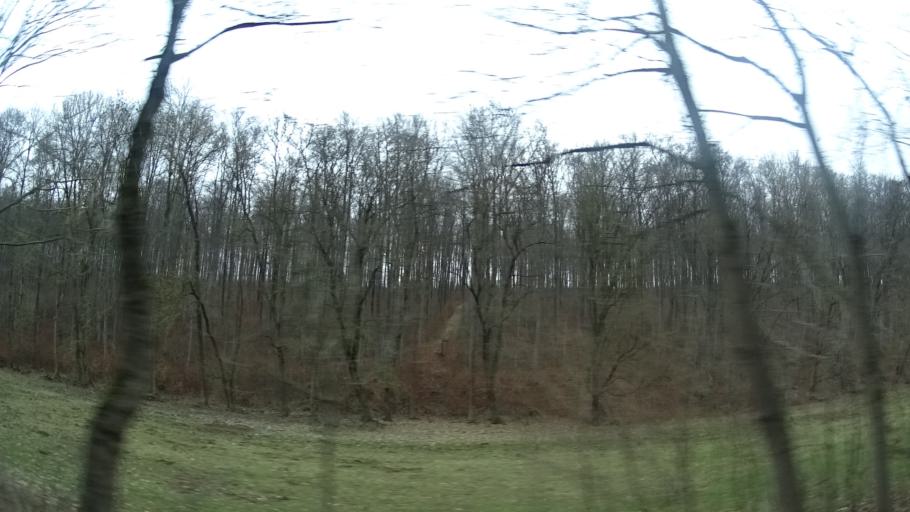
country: DE
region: Thuringia
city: Troistedt
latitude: 50.9143
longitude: 11.2311
